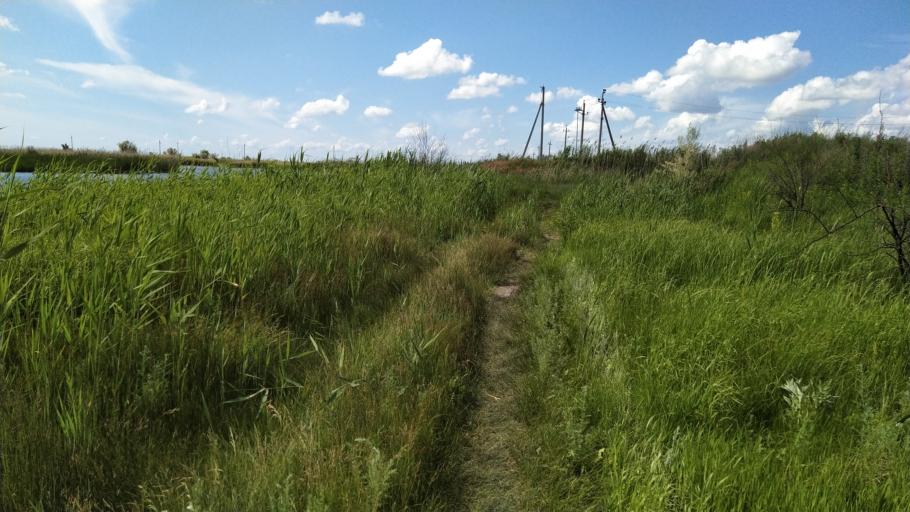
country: RU
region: Rostov
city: Bataysk
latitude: 47.1405
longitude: 39.6690
